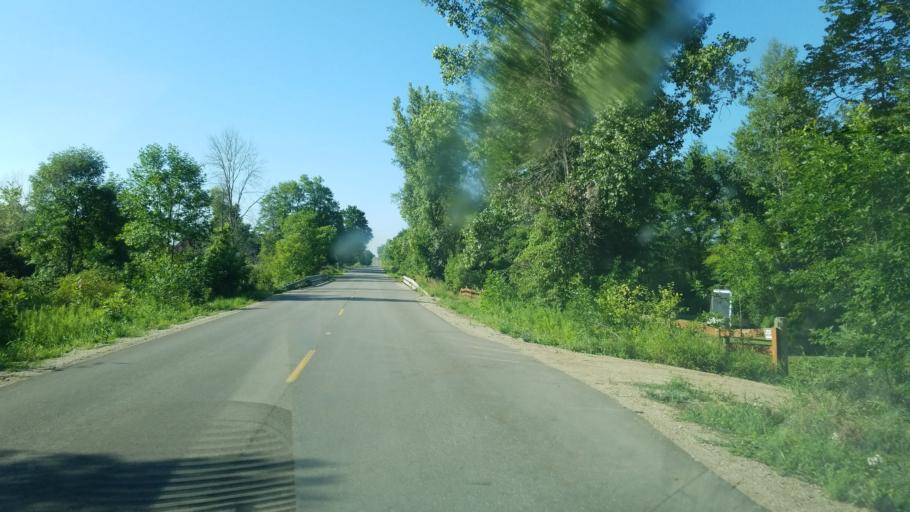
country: US
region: Michigan
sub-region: Mecosta County
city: Canadian Lakes
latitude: 43.5051
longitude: -85.3929
